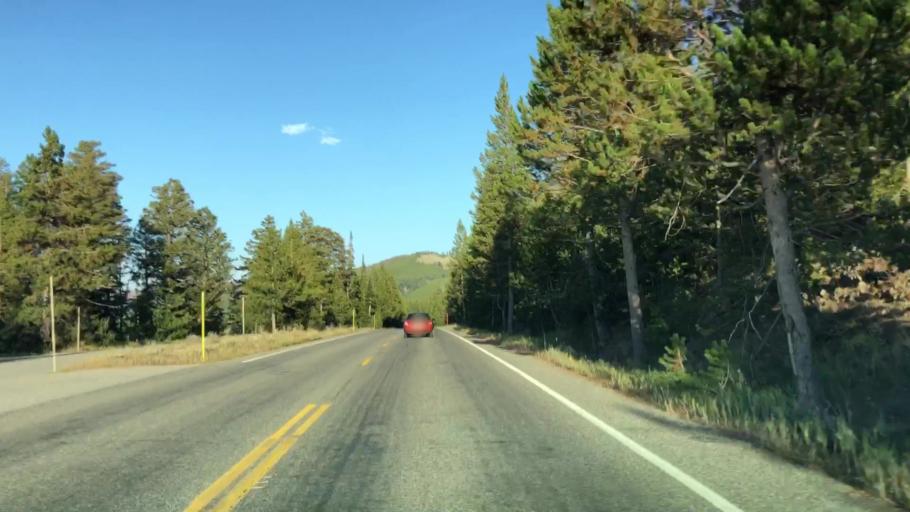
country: US
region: Montana
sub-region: Gallatin County
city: West Yellowstone
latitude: 44.6499
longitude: -111.0148
